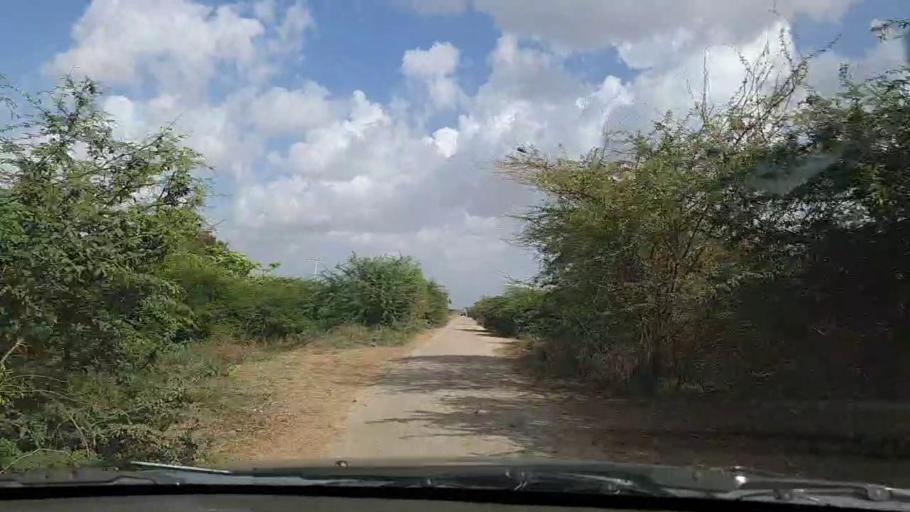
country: PK
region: Sindh
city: Keti Bandar
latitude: 24.0971
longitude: 67.6059
